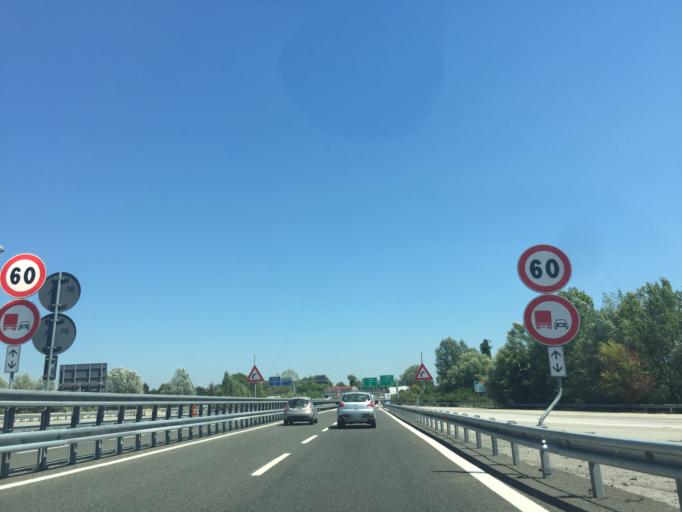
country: IT
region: Tuscany
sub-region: Provincia di Lucca
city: Lucca
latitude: 43.8364
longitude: 10.4699
